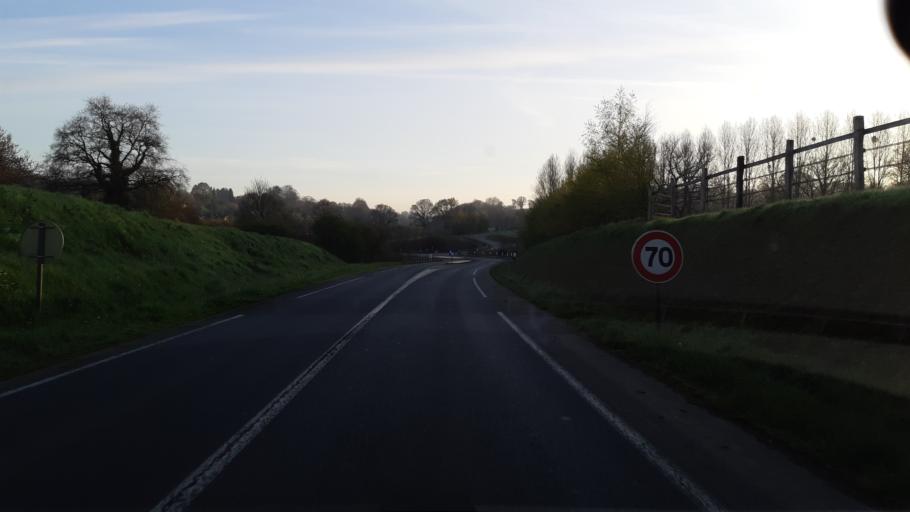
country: FR
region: Lower Normandy
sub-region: Departement de la Manche
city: Agneaux
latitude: 49.0679
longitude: -1.1309
